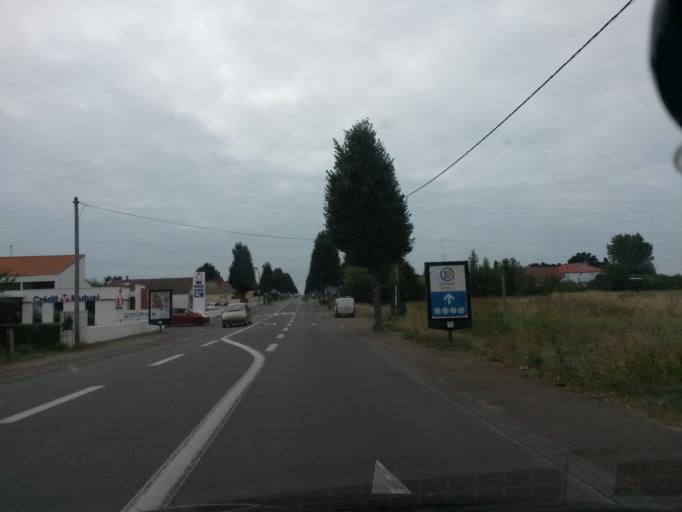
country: FR
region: Pays de la Loire
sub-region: Departement de la Vendee
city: Olonne-sur-Mer
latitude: 46.5313
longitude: -1.7741
